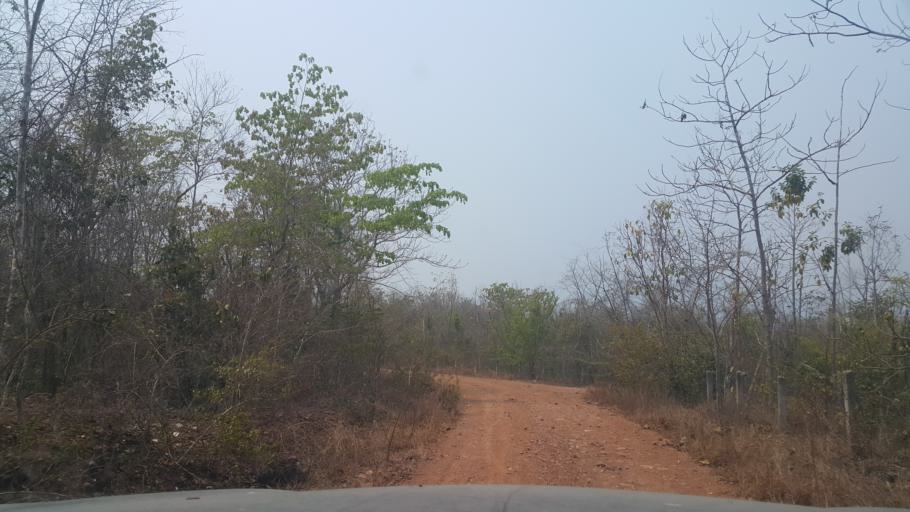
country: TH
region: Lampang
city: Sop Prap
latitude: 17.8906
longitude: 99.3193
